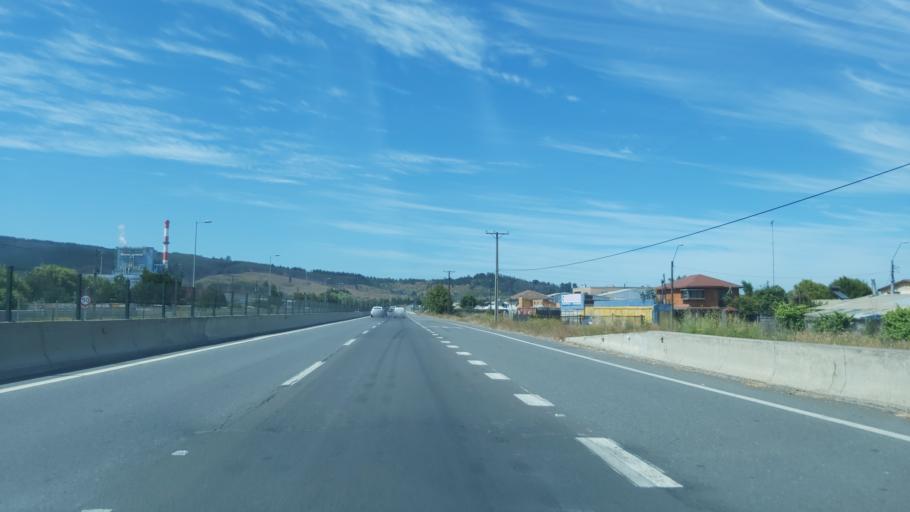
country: CL
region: Biobio
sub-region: Provincia de Concepcion
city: Coronel
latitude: -37.0331
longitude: -73.1349
